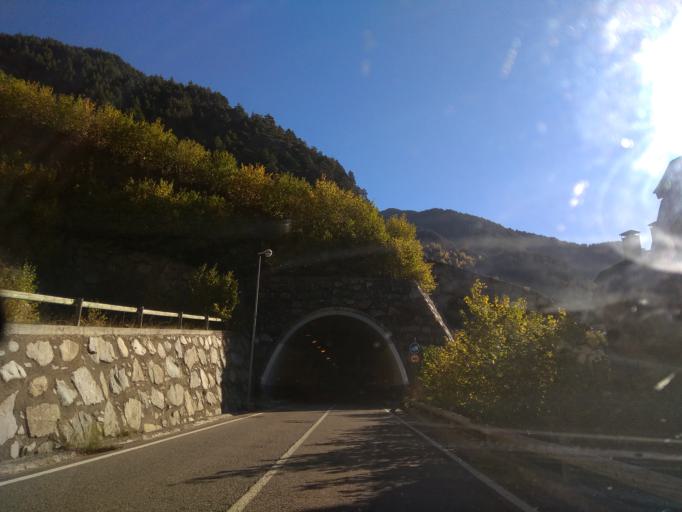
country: AD
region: La Massana
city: Arinsal
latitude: 42.5802
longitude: 1.4778
